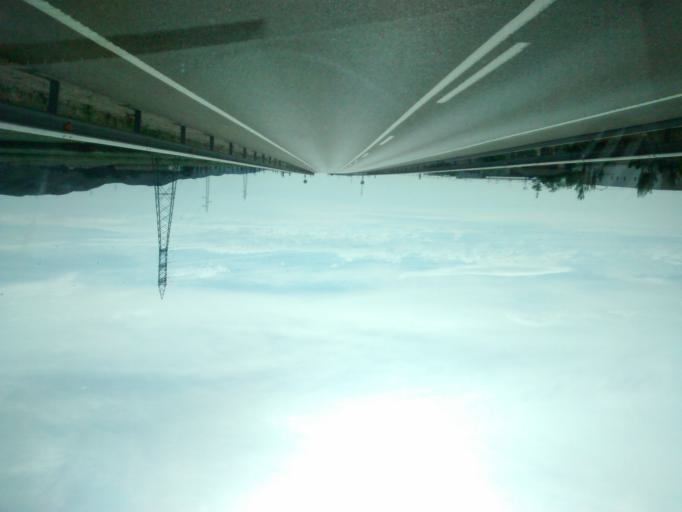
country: ES
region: Aragon
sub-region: Provincia de Zaragoza
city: El Burgo de Ebro
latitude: 41.5627
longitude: -0.7332
